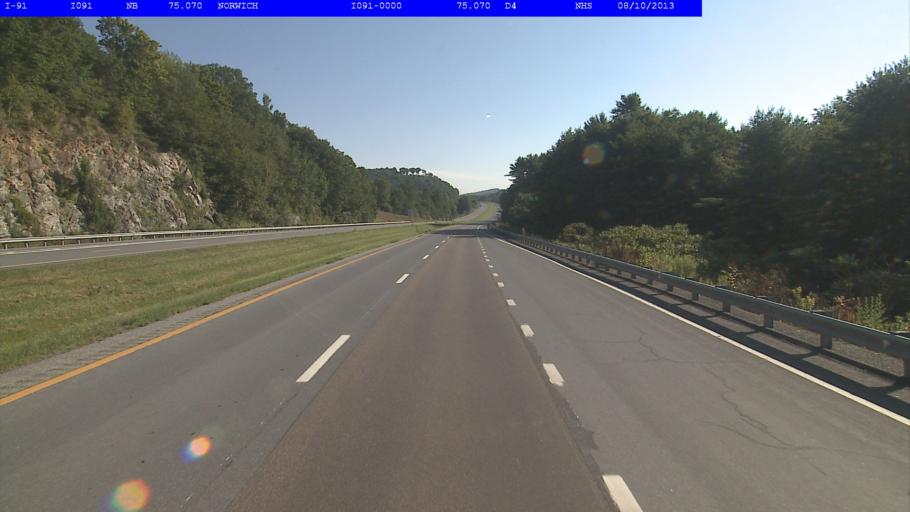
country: US
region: New Hampshire
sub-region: Grafton County
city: Hanover
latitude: 43.7085
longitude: -72.3034
